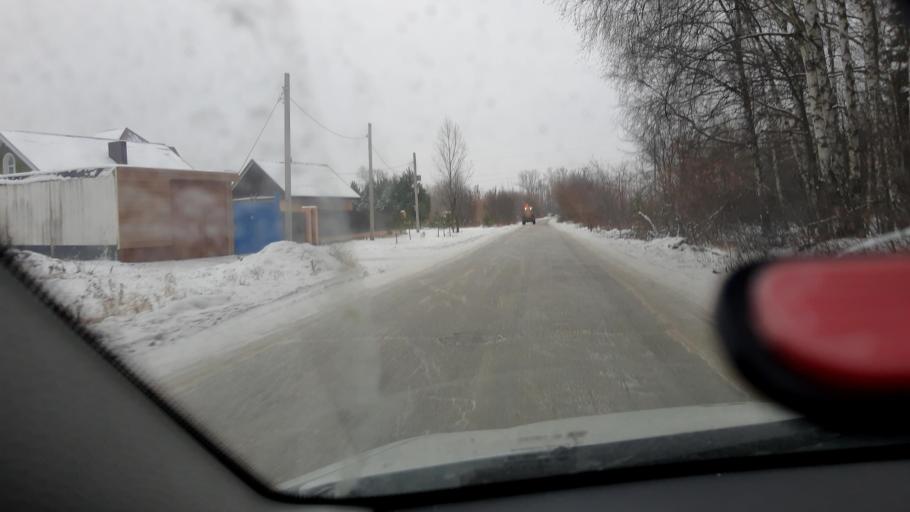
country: RU
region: Bashkortostan
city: Ufa
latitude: 54.7893
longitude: 56.1586
